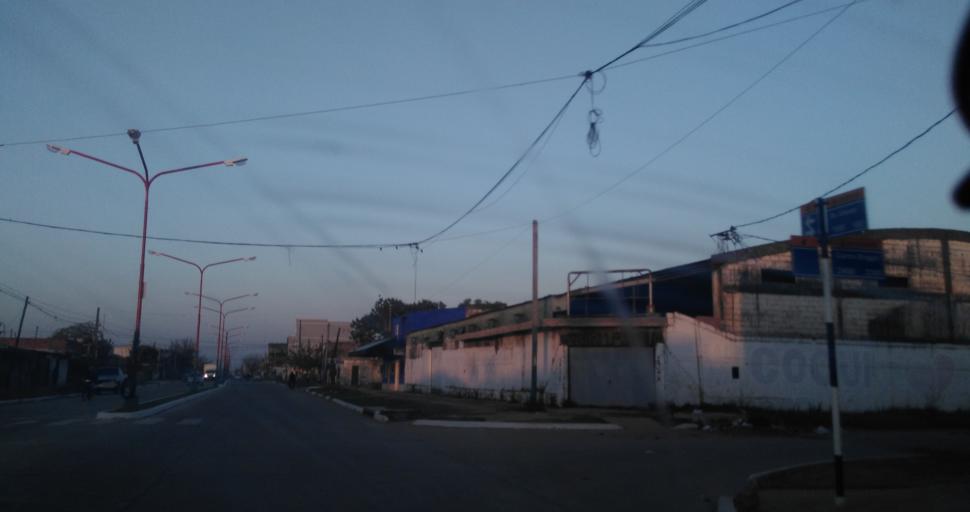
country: AR
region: Chaco
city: Resistencia
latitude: -27.4780
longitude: -58.9737
